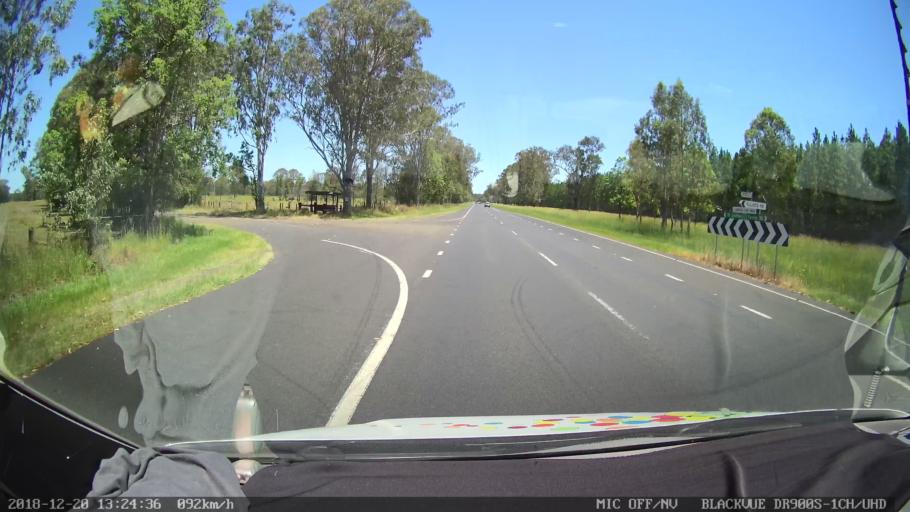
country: AU
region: New South Wales
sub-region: Richmond Valley
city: Casino
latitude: -29.1196
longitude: 152.9997
